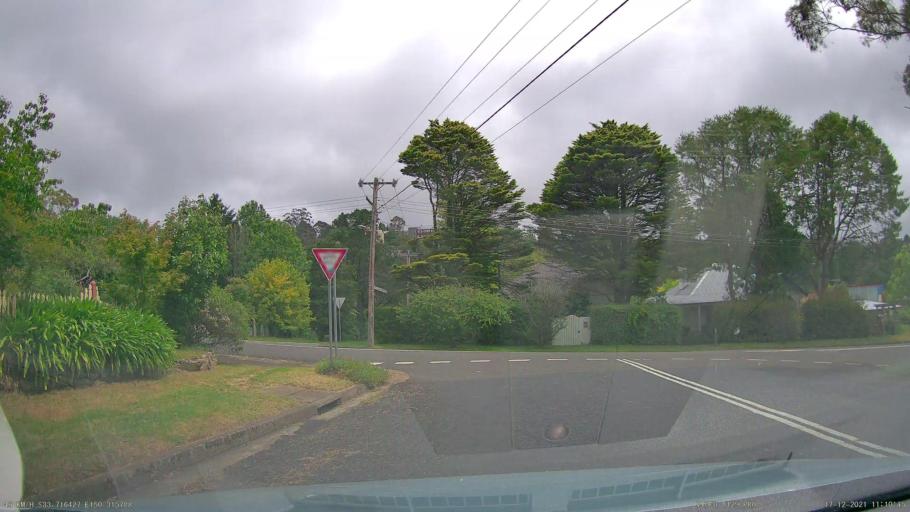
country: AU
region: New South Wales
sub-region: Blue Mountains Municipality
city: Katoomba
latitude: -33.7163
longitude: 150.3157
